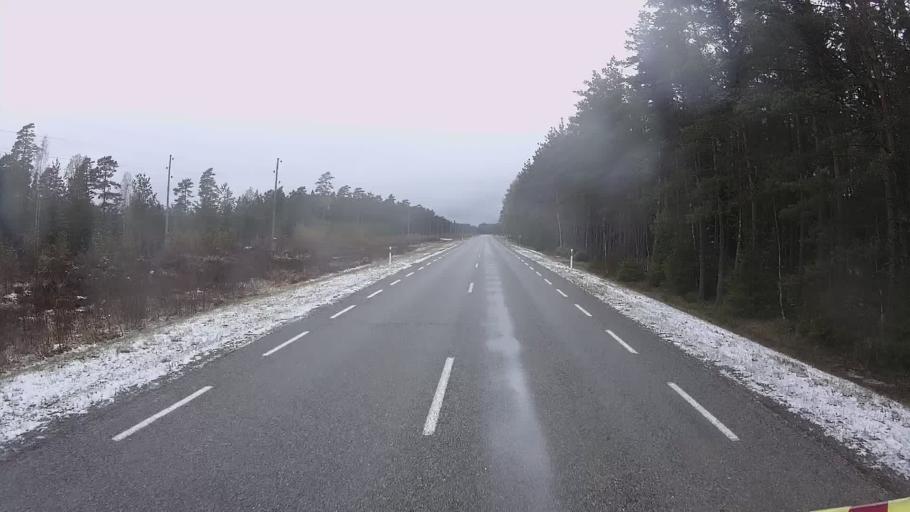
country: EE
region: Hiiumaa
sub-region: Kaerdla linn
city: Kardla
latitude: 59.0190
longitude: 22.6721
